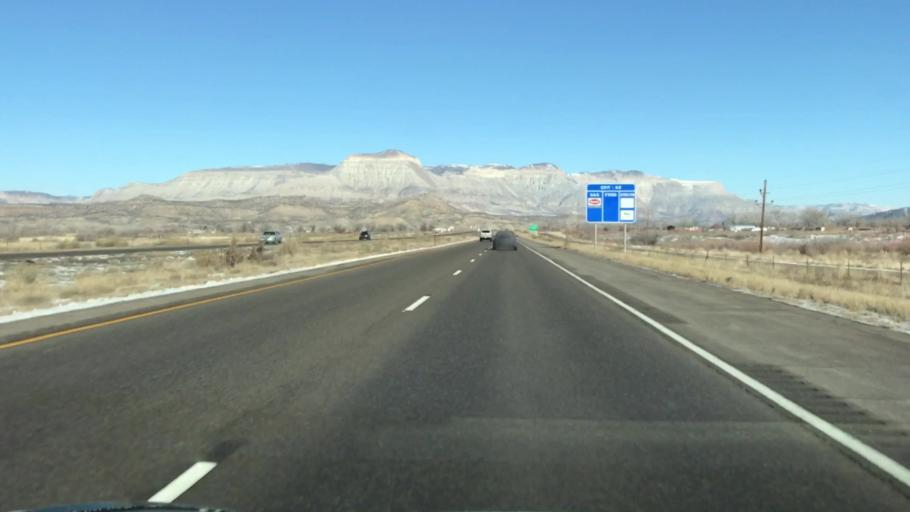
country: US
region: Colorado
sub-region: Garfield County
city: Parachute
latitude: 39.3049
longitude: -108.2174
